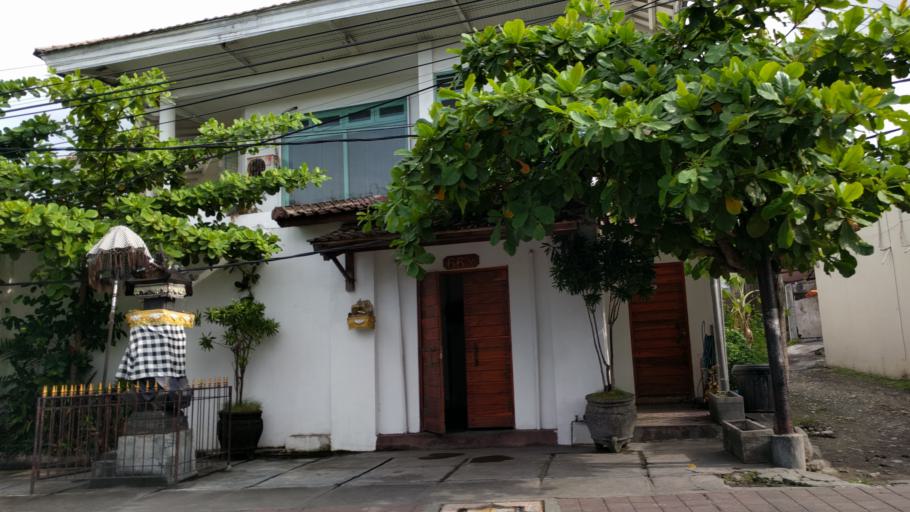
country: ID
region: Bali
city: Kuta
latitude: -8.6840
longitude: 115.1620
